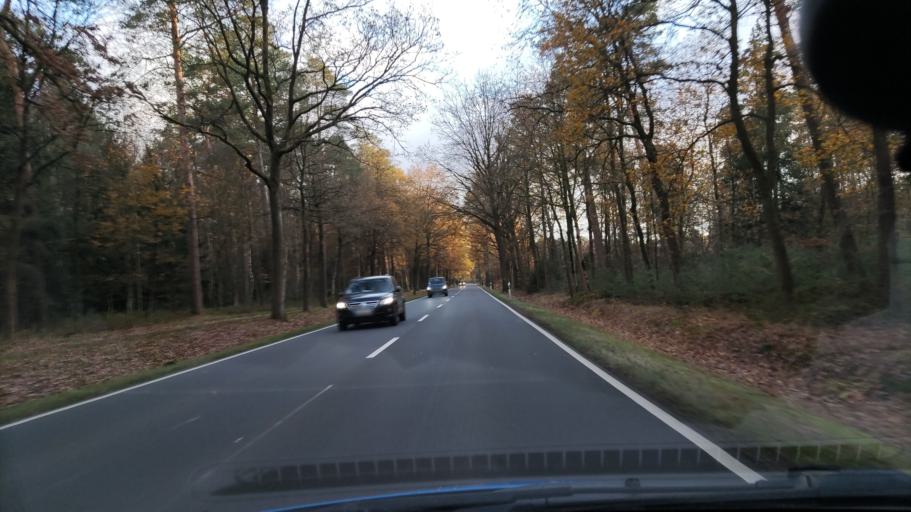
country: DE
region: Lower Saxony
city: Neuenkirchen
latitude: 53.0182
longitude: 9.7751
